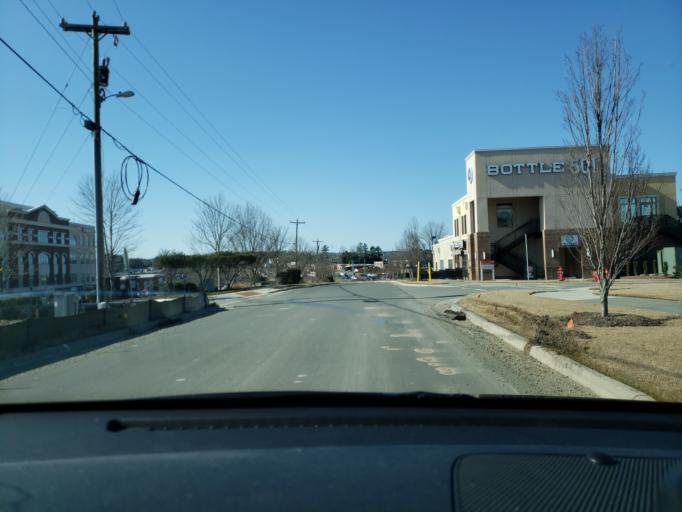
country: US
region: North Carolina
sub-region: Orange County
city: Chapel Hill
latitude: 35.9528
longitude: -78.9913
